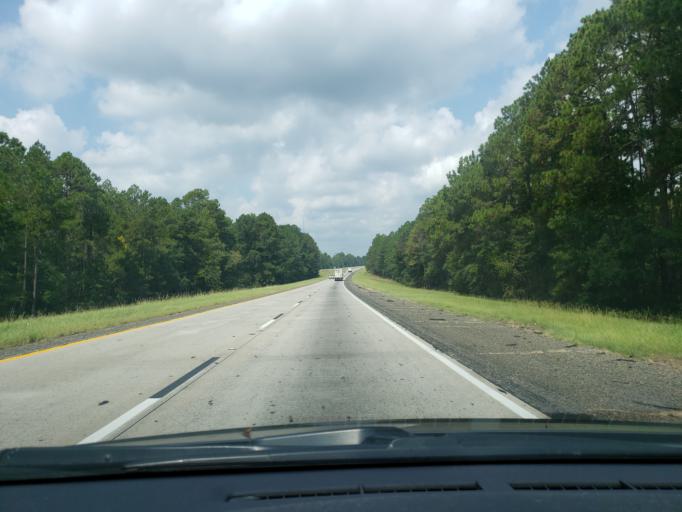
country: US
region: Georgia
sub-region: Treutlen County
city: Soperton
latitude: 32.4353
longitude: -82.6490
